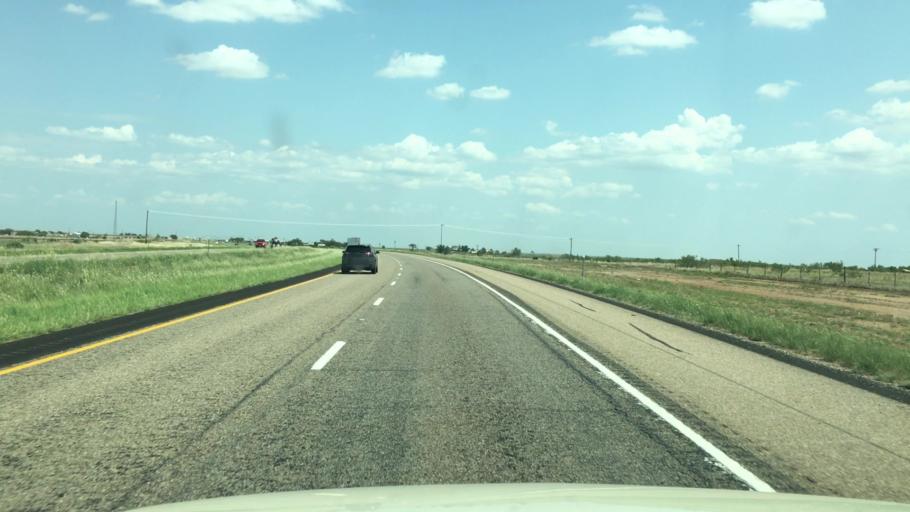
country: US
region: Texas
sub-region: Armstrong County
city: Claude
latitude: 35.0351
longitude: -101.1981
